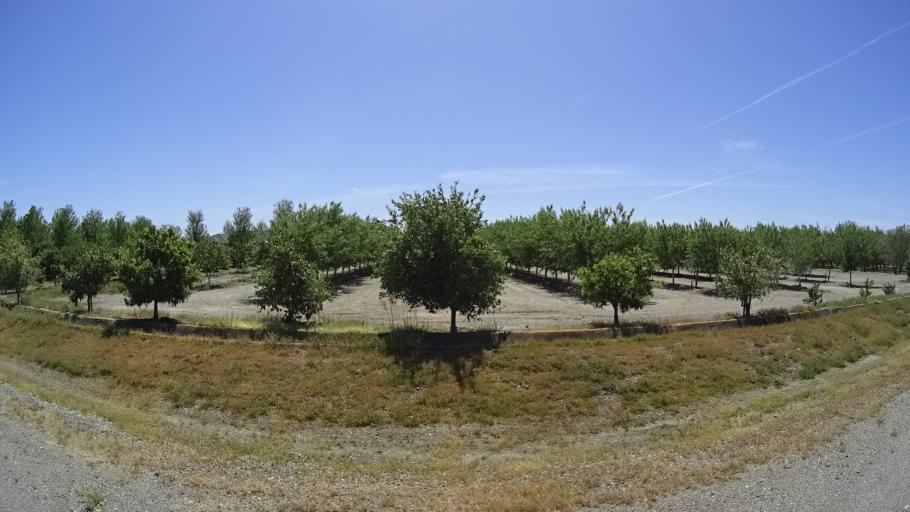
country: US
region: California
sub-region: Glenn County
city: Orland
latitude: 39.7251
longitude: -122.1272
